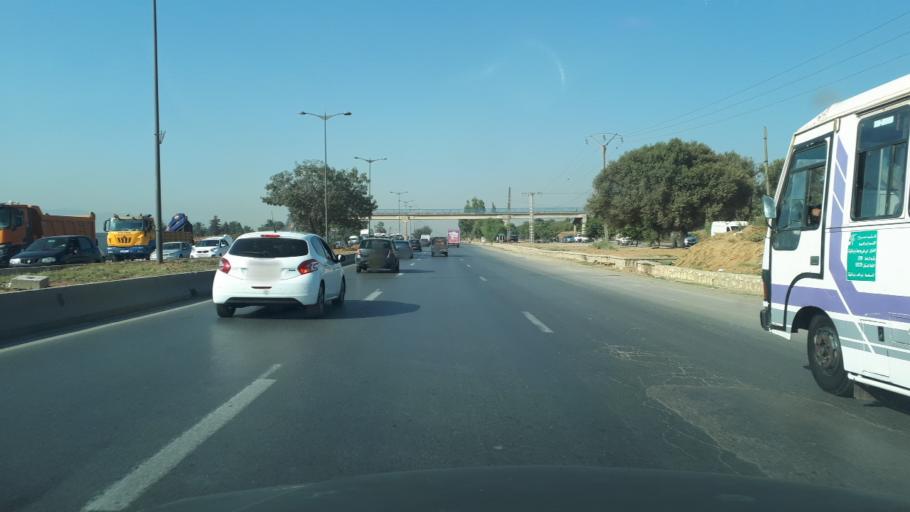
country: DZ
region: Tipaza
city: Saoula
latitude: 36.6682
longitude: 3.0432
